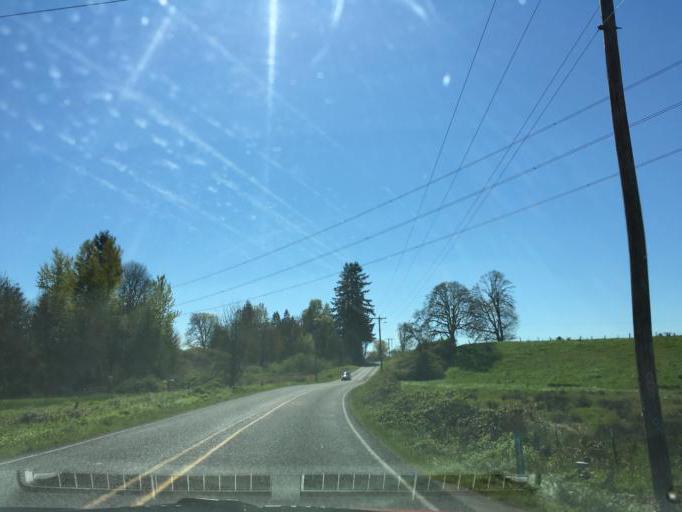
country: US
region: Oregon
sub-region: Marion County
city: Hubbard
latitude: 45.1512
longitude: -122.7244
